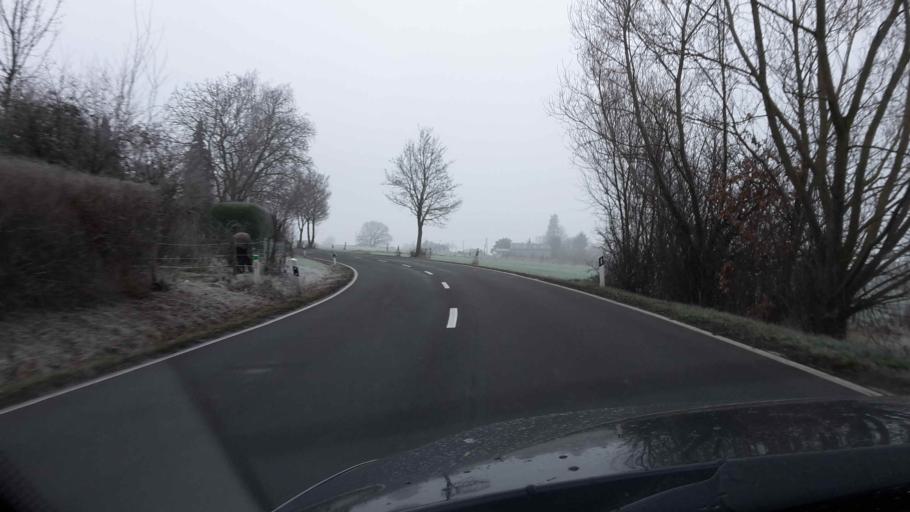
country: DE
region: North Rhine-Westphalia
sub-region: Regierungsbezirk Koln
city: Hennef
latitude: 50.7326
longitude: 7.2907
